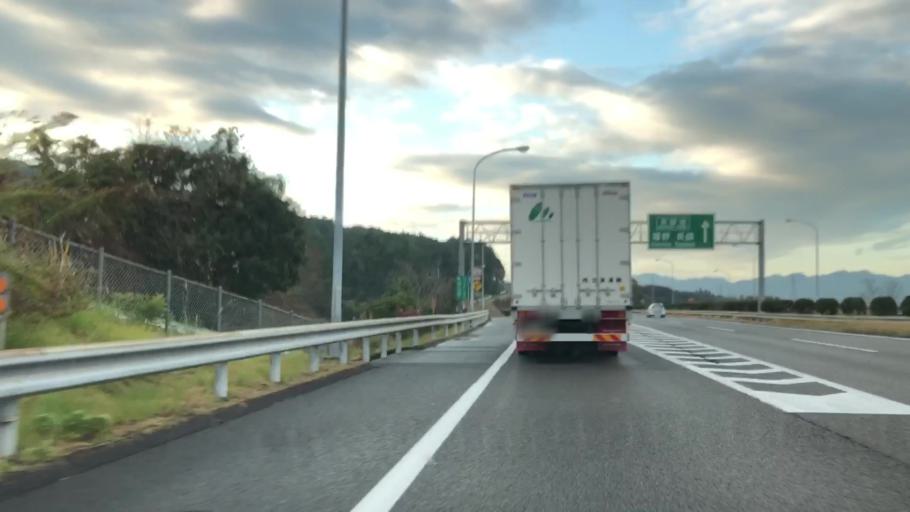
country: JP
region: Saga Prefecture
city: Ureshinomachi-shimojuku
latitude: 33.1498
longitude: 129.9996
